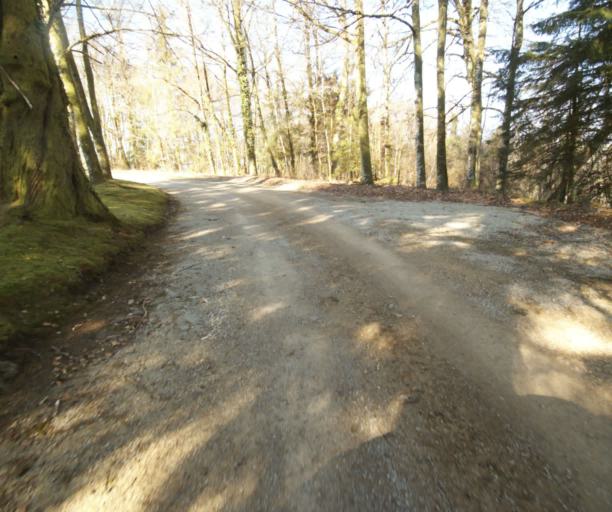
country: FR
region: Limousin
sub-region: Departement de la Correze
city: Correze
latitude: 45.3006
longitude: 1.8640
